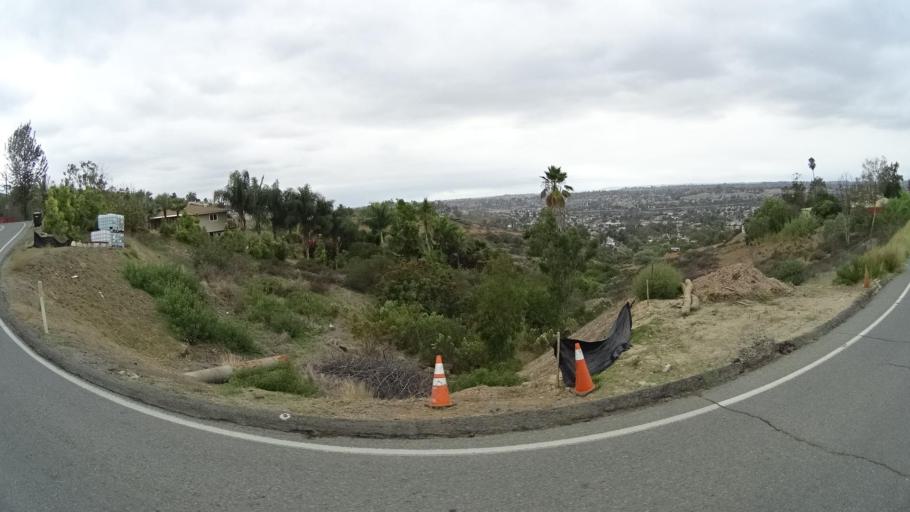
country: US
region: California
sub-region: San Diego County
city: Spring Valley
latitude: 32.7313
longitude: -116.9978
